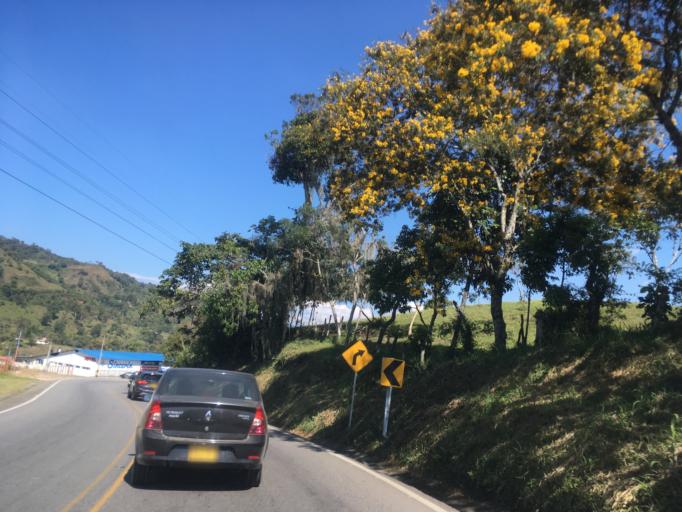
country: CO
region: Santander
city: Suaita
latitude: 6.0658
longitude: -73.4262
